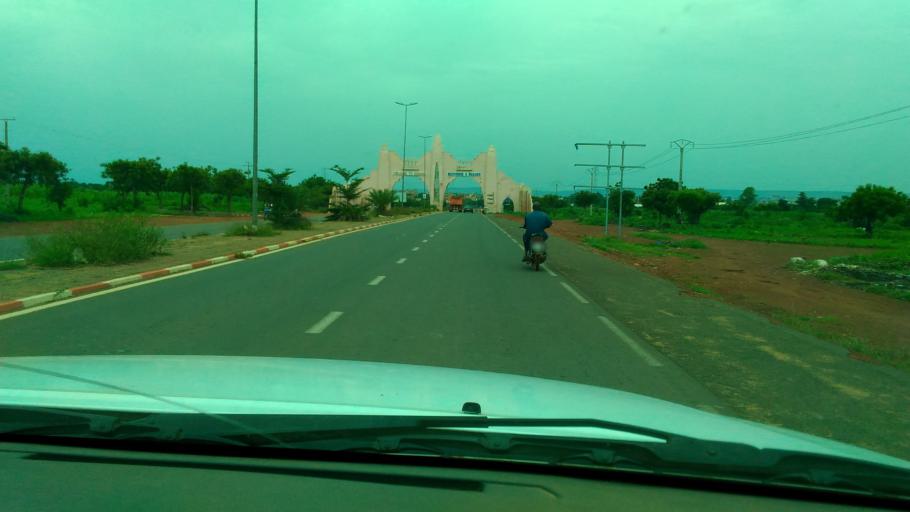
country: ML
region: Bamako
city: Bamako
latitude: 12.5566
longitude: -7.9725
